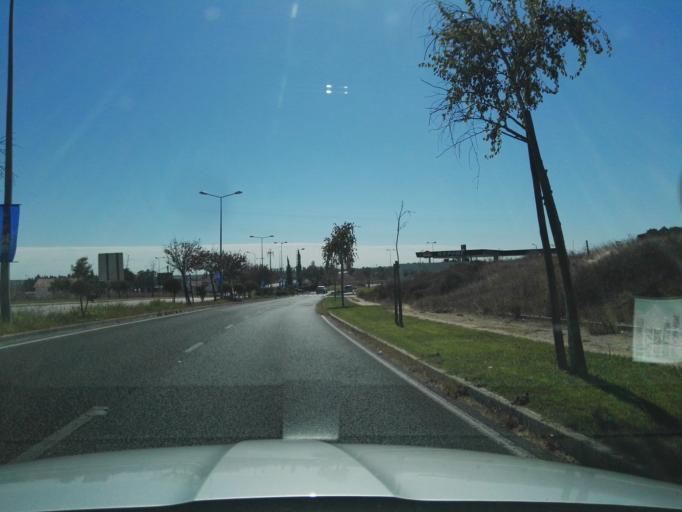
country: PT
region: Setubal
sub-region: Alcochete
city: Alcochete
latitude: 38.7466
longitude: -8.9312
